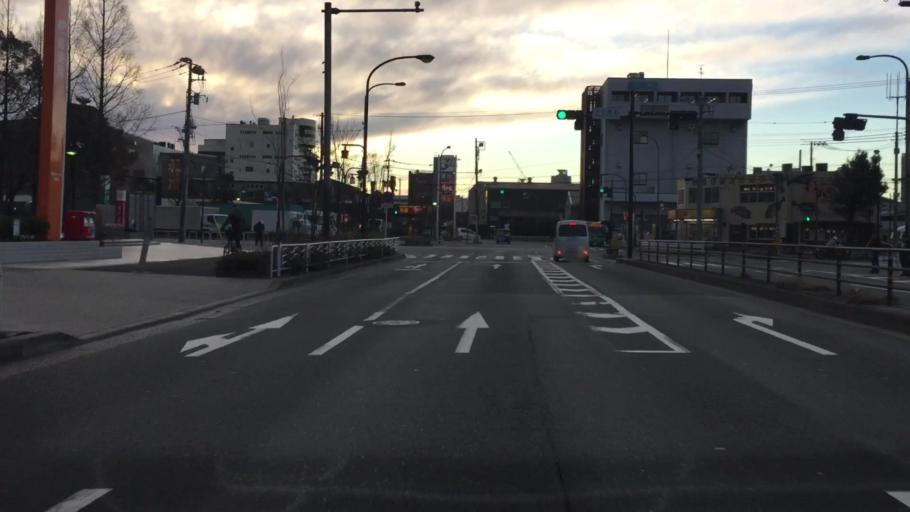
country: JP
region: Tokyo
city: Urayasu
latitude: 35.6445
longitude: 139.8260
